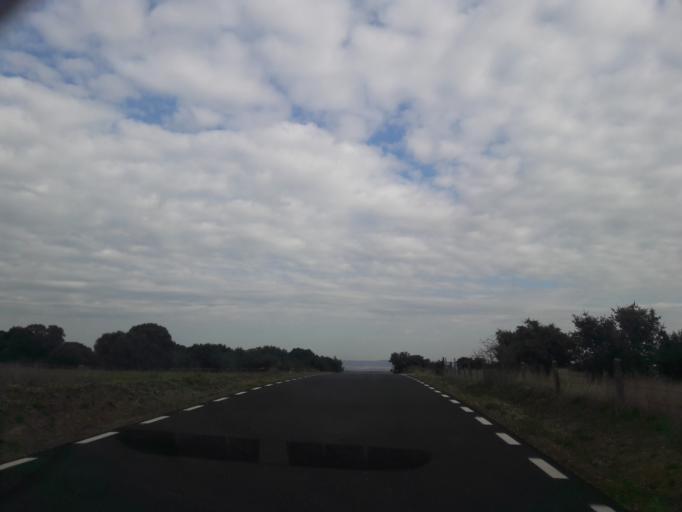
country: ES
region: Castille and Leon
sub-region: Provincia de Salamanca
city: Pastores
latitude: 40.5106
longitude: -6.5287
